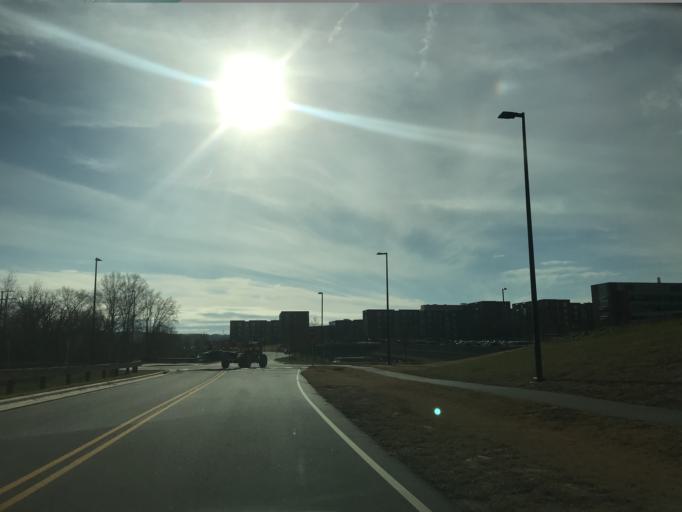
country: US
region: North Carolina
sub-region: Wake County
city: West Raleigh
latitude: 35.7715
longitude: -78.6705
